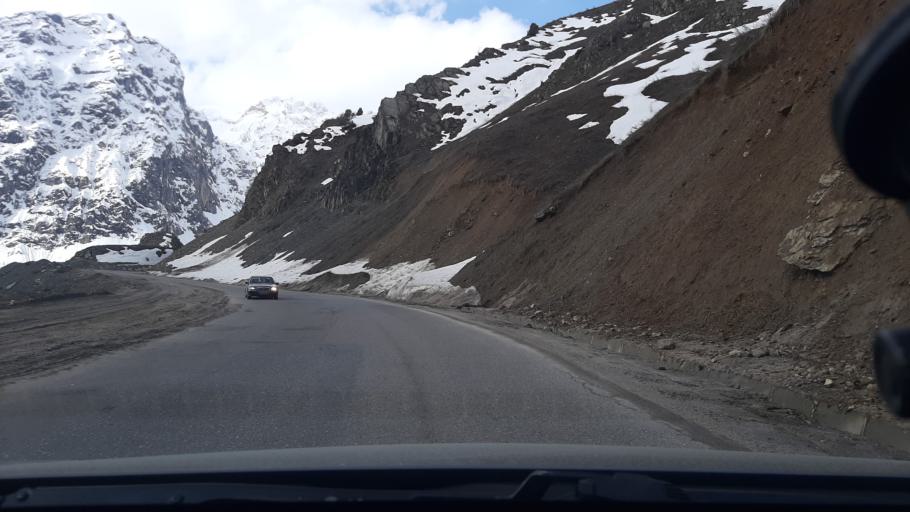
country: TJ
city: Tagob
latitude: 39.0515
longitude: 68.7437
